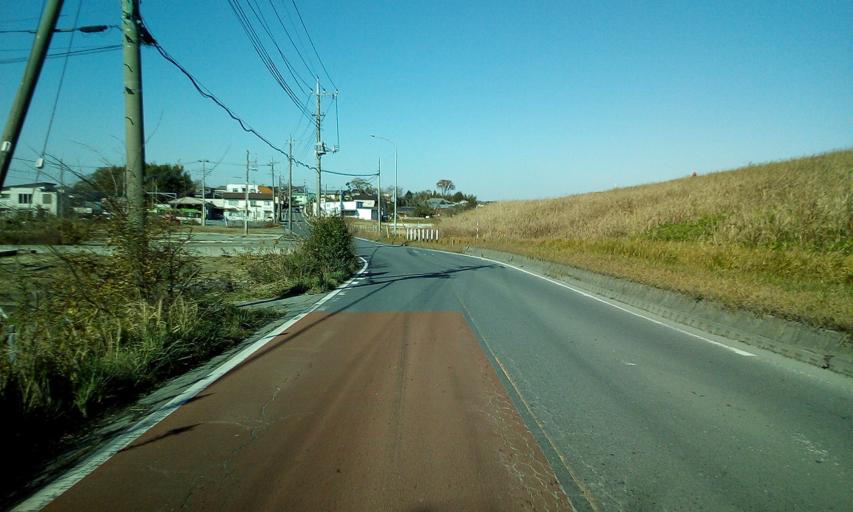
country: JP
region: Chiba
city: Noda
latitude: 35.9442
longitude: 139.8402
